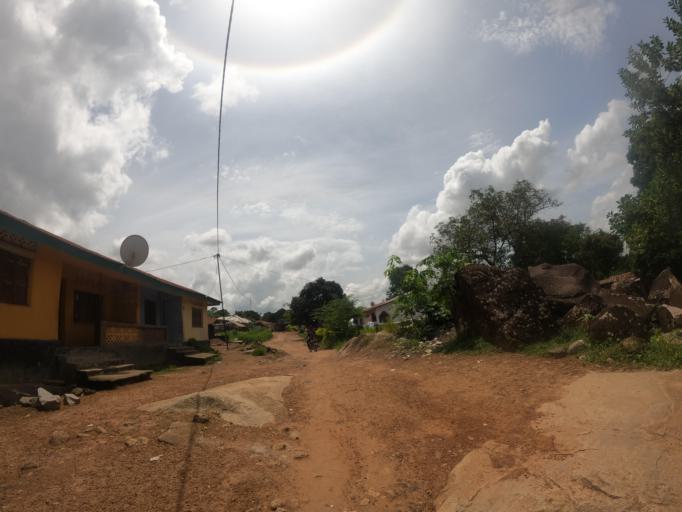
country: SL
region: Northern Province
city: Makeni
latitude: 8.8989
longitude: -12.0541
